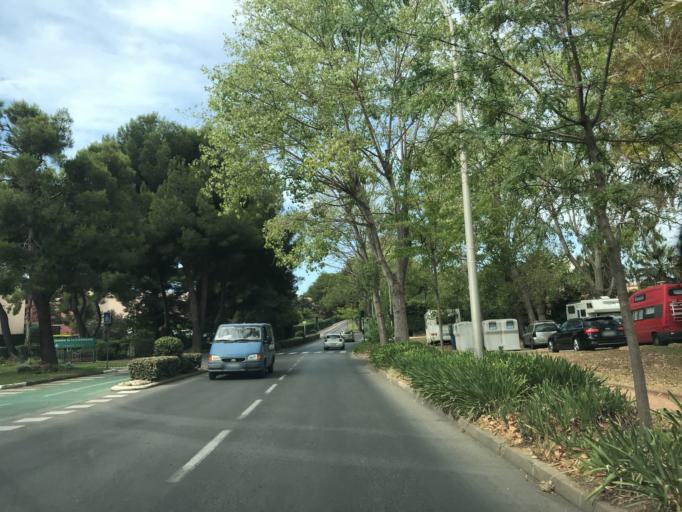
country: FR
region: Provence-Alpes-Cote d'Azur
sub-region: Departement du Var
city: Sanary-sur-Mer
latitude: 43.0999
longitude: 5.8158
